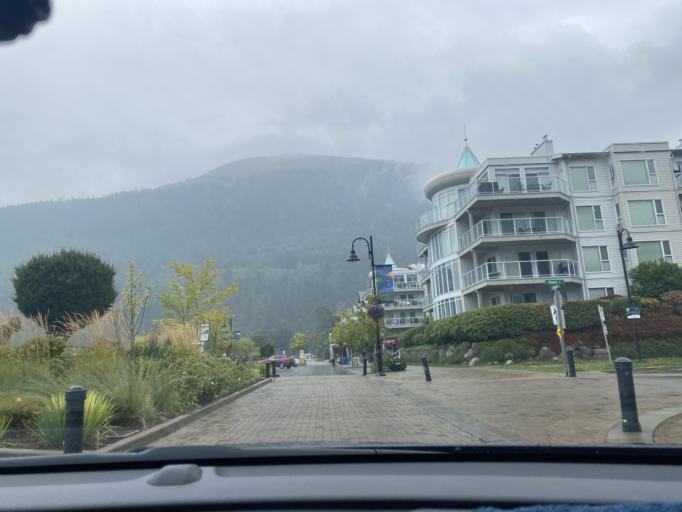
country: CA
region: British Columbia
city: Agassiz
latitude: 49.3031
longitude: -121.7831
